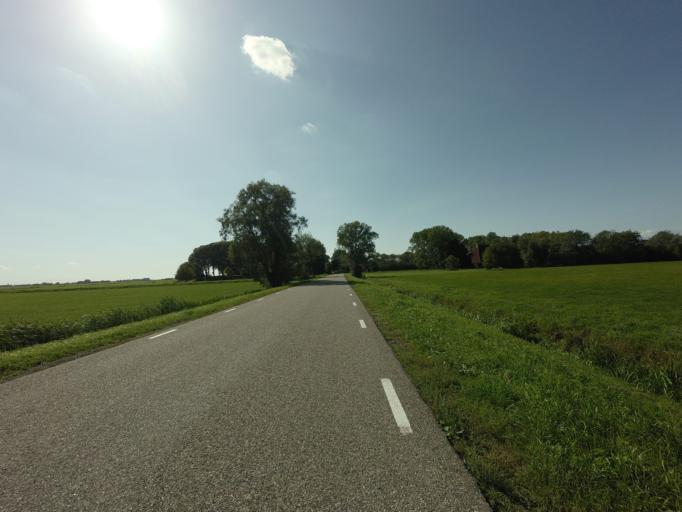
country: NL
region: Friesland
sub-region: Gemeente Littenseradiel
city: Makkum
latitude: 53.1137
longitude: 5.6789
